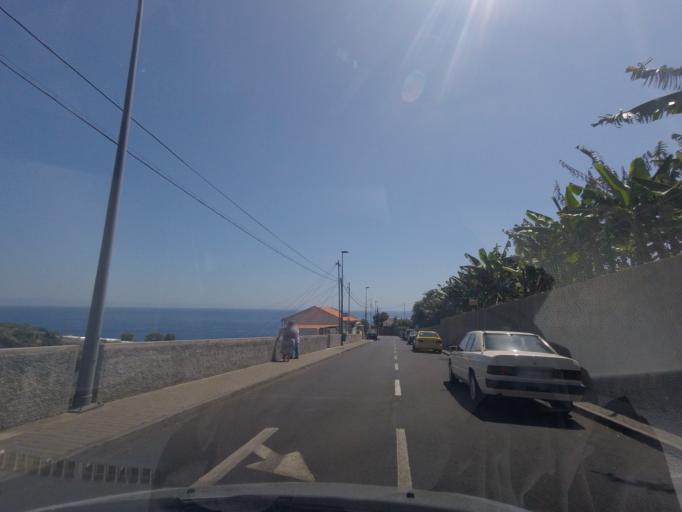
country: PT
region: Madeira
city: Camara de Lobos
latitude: 32.6487
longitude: -16.9611
